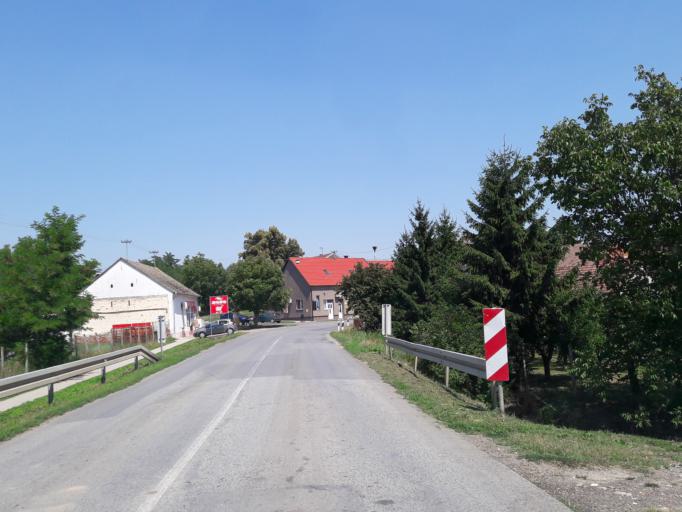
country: HR
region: Osjecko-Baranjska
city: Viskovci
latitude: 45.3447
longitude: 18.4576
